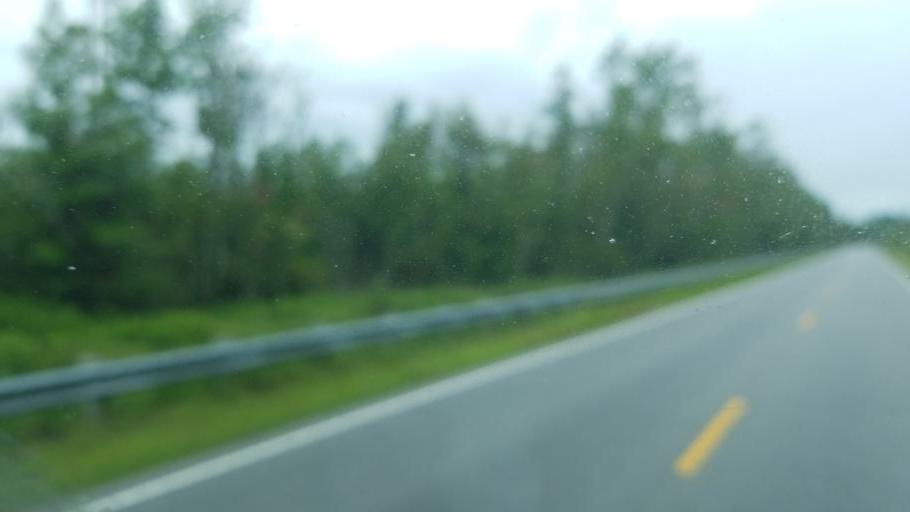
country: US
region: North Carolina
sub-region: Tyrrell County
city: Columbia
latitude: 35.9075
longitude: -76.1040
